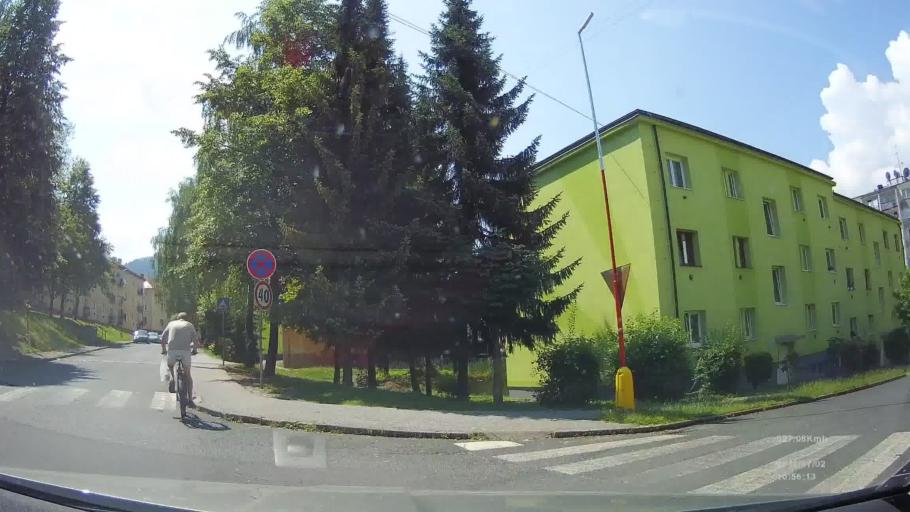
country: SK
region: Kosicky
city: Krompachy
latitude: 48.9151
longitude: 20.8758
